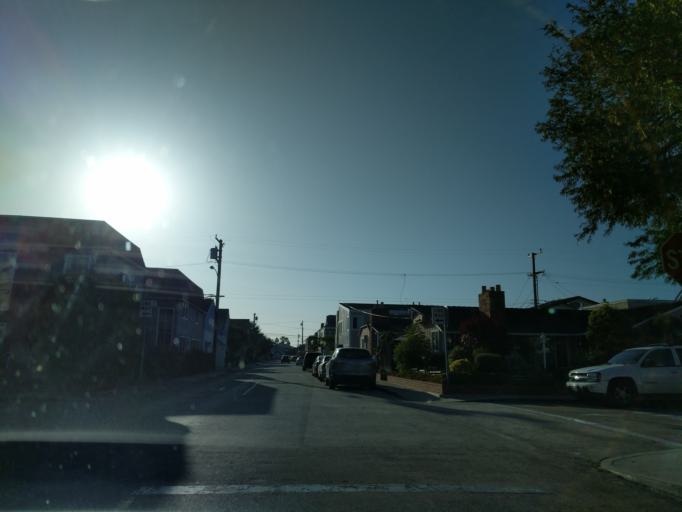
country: US
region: California
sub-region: Orange County
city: Newport Beach
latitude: 33.6070
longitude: -117.8925
